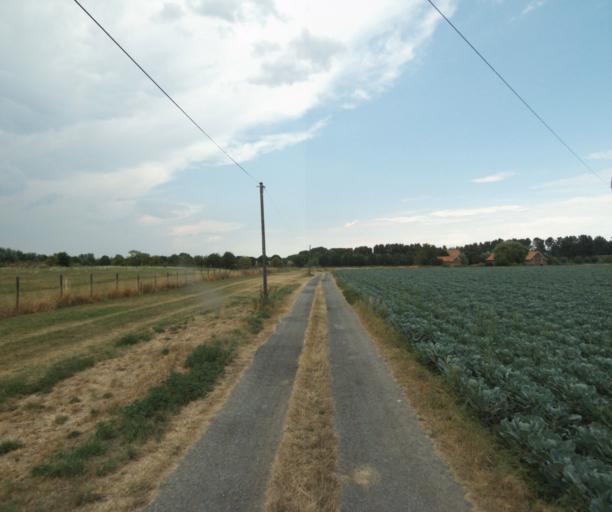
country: FR
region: Nord-Pas-de-Calais
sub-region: Departement du Nord
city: Deulemont
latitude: 50.7196
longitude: 2.9626
